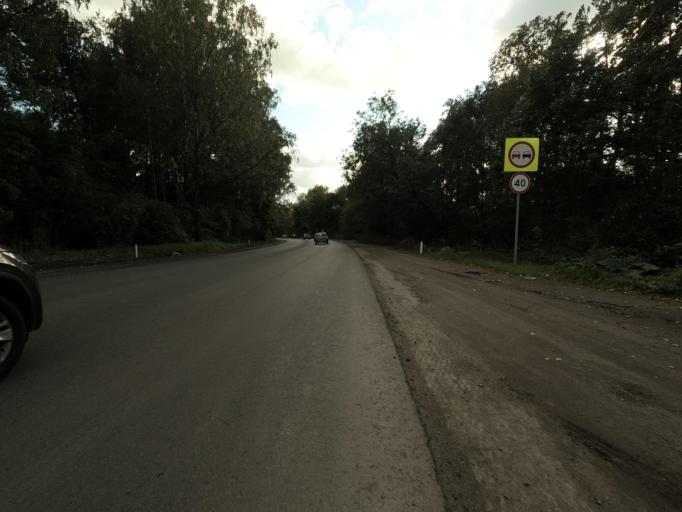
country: RU
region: Leningrad
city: Koltushi
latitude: 59.9444
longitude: 30.6560
